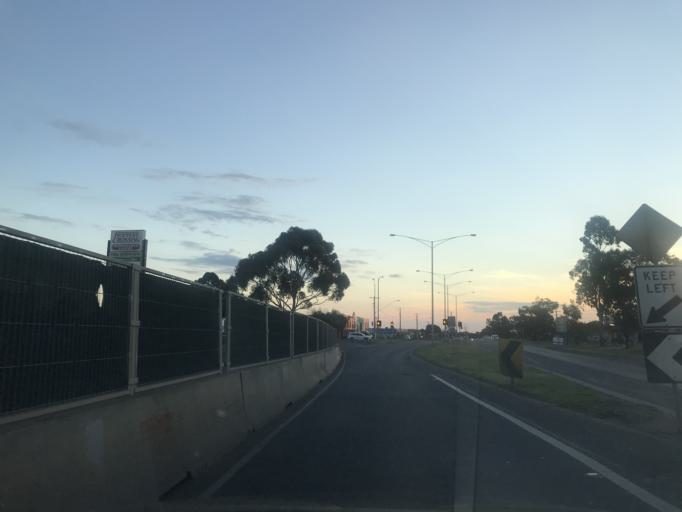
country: AU
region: Victoria
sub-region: Wyndham
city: Williams Landing
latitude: -37.8691
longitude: 144.7311
